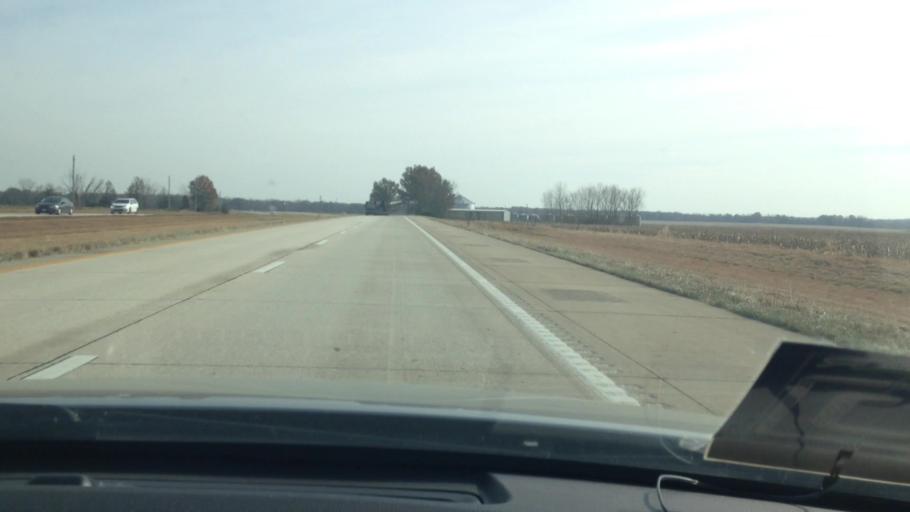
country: US
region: Missouri
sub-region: Henry County
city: Clinton
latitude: 38.4308
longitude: -93.9259
